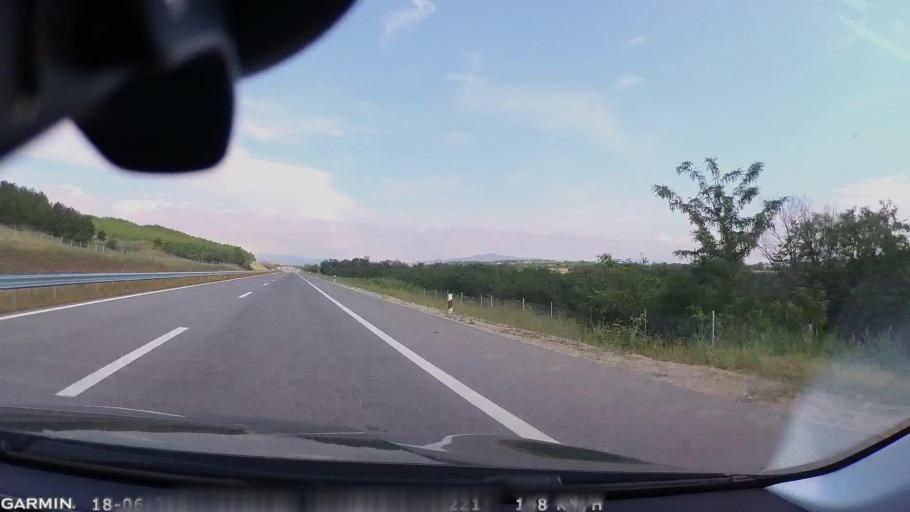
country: MK
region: Sveti Nikole
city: Sveti Nikole
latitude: 41.8973
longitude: 21.9200
